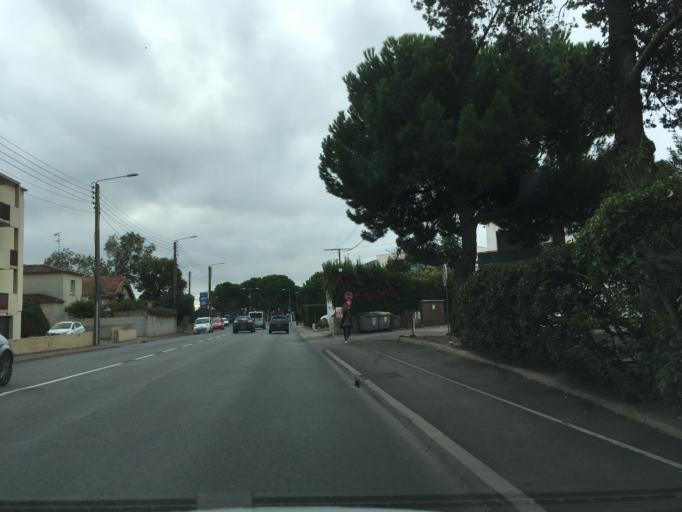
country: FR
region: Languedoc-Roussillon
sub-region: Departement de l'Herault
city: Montpellier
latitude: 43.5925
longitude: 3.8897
